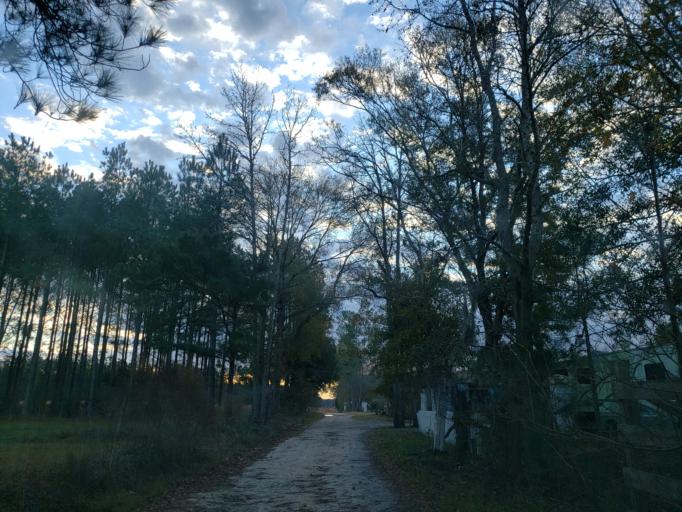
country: US
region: Georgia
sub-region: Chatham County
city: Bloomingdale
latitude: 32.1125
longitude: -81.3437
